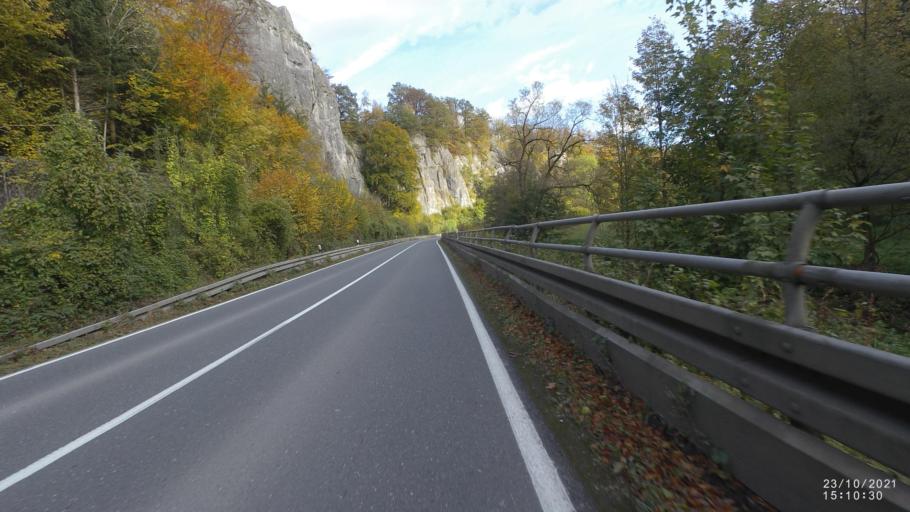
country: DE
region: North Rhine-Westphalia
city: Balve
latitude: 51.3788
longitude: 7.8550
